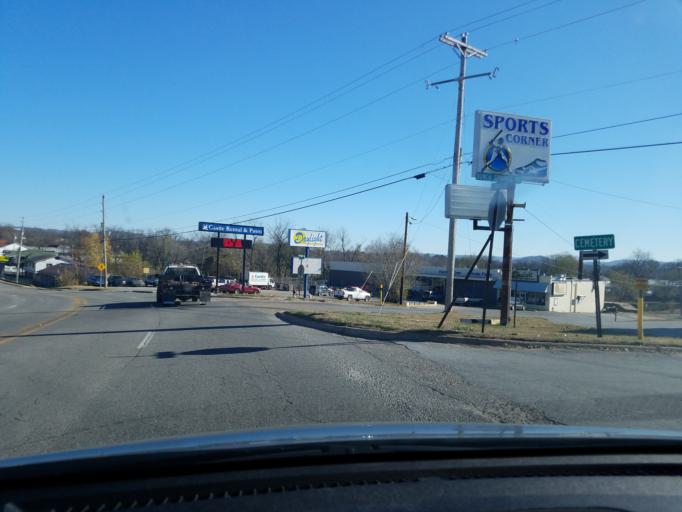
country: US
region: Arkansas
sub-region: Carroll County
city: Berryville
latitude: 36.3673
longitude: -93.5779
